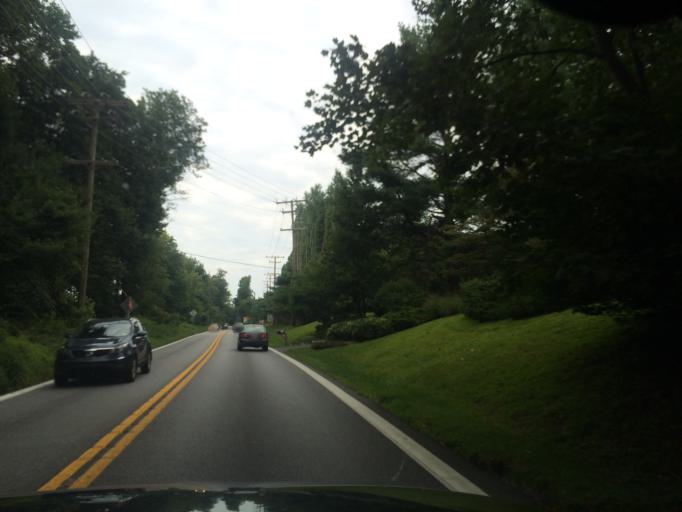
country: US
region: Maryland
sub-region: Carroll County
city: Sykesville
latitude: 39.3483
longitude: -77.0151
